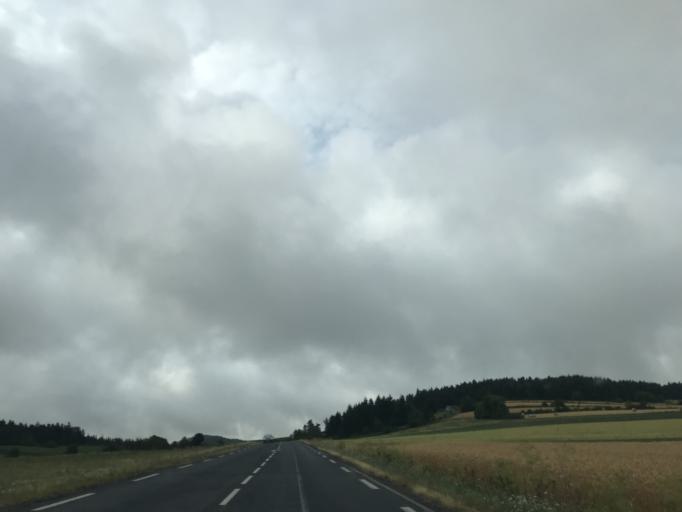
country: FR
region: Auvergne
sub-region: Departement de la Haute-Loire
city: Saint-Paulien
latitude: 45.1766
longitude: 3.8272
